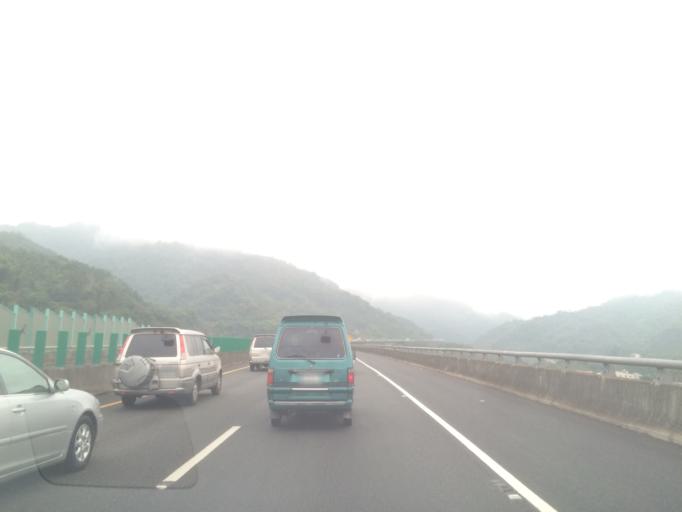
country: TW
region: Taiwan
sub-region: Nantou
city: Puli
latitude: 23.9835
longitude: 120.8626
